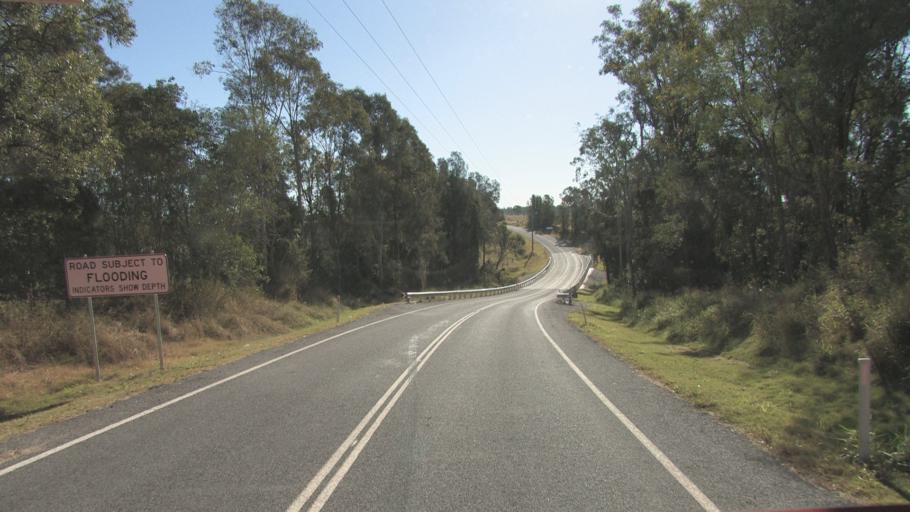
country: AU
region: Queensland
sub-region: Logan
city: Chambers Flat
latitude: -27.7736
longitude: 153.0727
